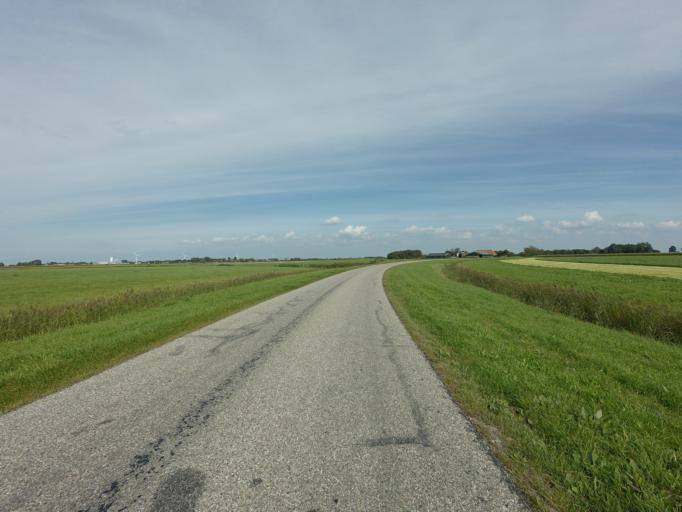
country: NL
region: Friesland
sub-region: Gemeente Franekeradeel
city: Franeker
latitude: 53.1673
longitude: 5.4994
